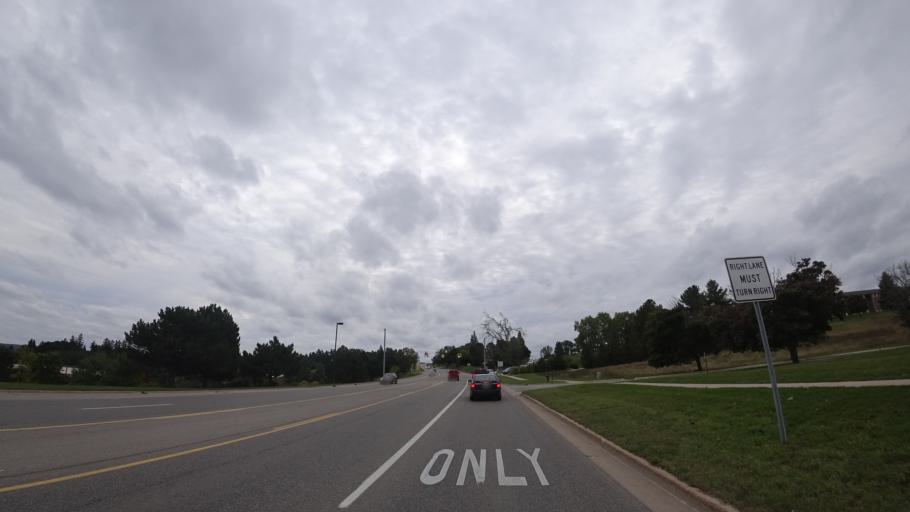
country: US
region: Michigan
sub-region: Emmet County
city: Petoskey
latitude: 45.3608
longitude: -84.9709
